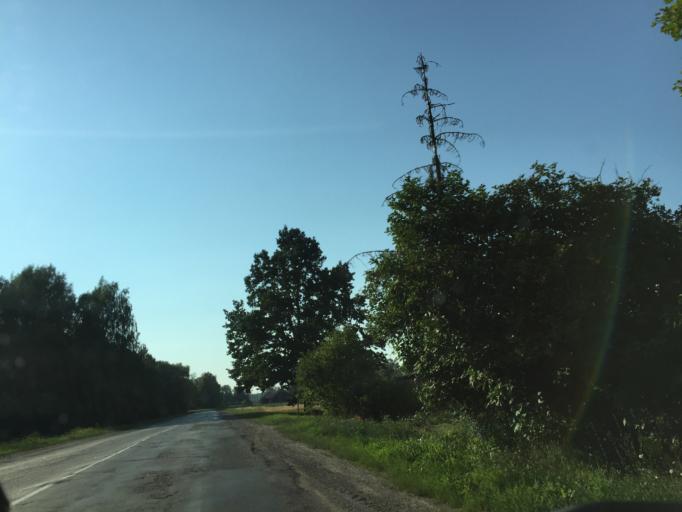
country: LV
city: Tervete
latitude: 56.4197
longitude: 23.5606
